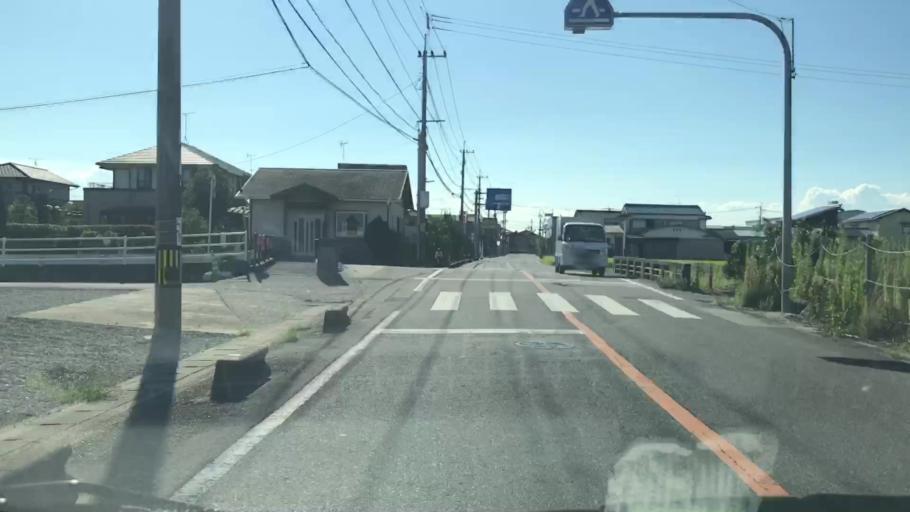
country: JP
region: Saga Prefecture
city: Okawa
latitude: 33.1894
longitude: 130.3219
